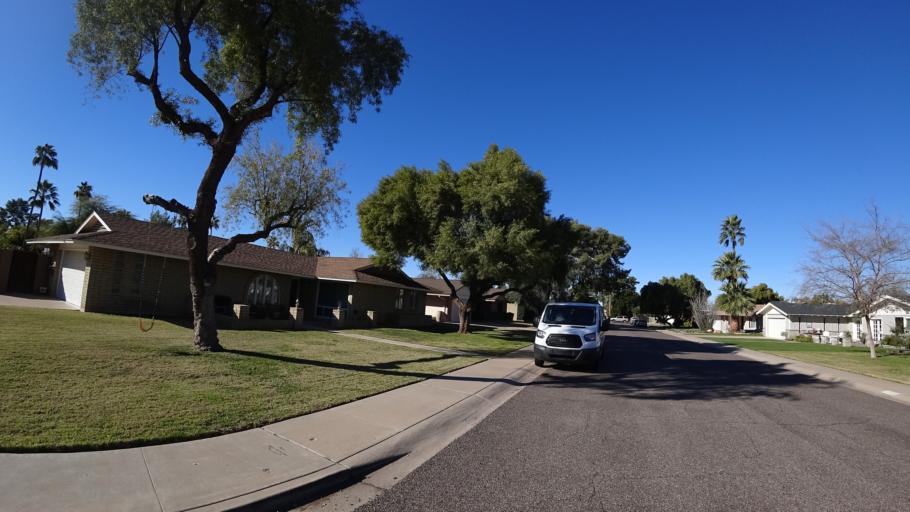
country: US
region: Arizona
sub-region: Maricopa County
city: Paradise Valley
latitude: 33.5032
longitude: -112.0070
